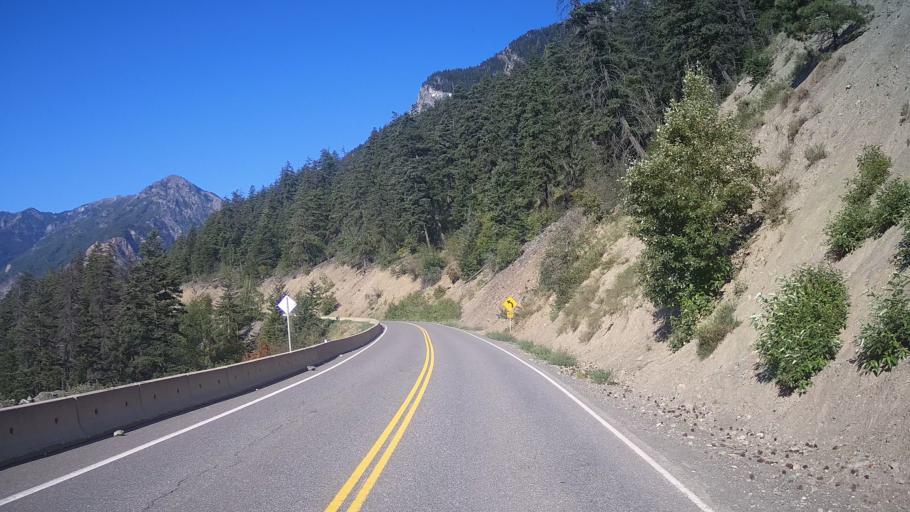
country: CA
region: British Columbia
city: Lillooet
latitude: 50.6548
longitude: -122.0108
